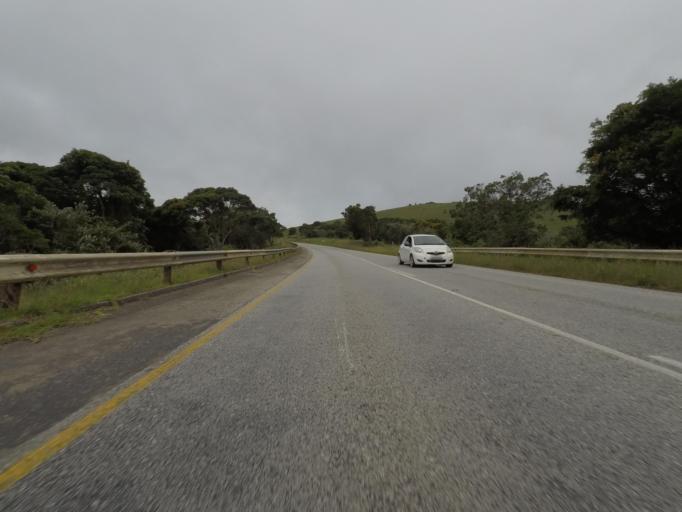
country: ZA
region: Eastern Cape
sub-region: Cacadu District Municipality
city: Port Alfred
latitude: -33.6140
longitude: 26.8032
